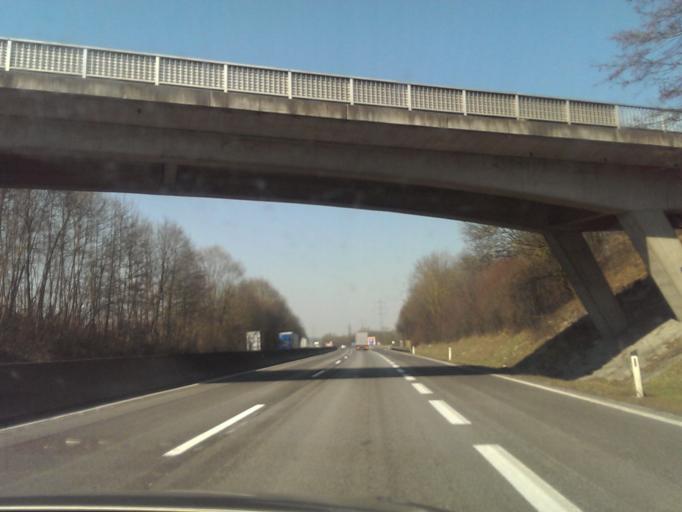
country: AT
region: Upper Austria
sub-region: Politischer Bezirk Vocklabruck
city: Wolfsegg am Hausruck
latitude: 48.2060
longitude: 13.6358
